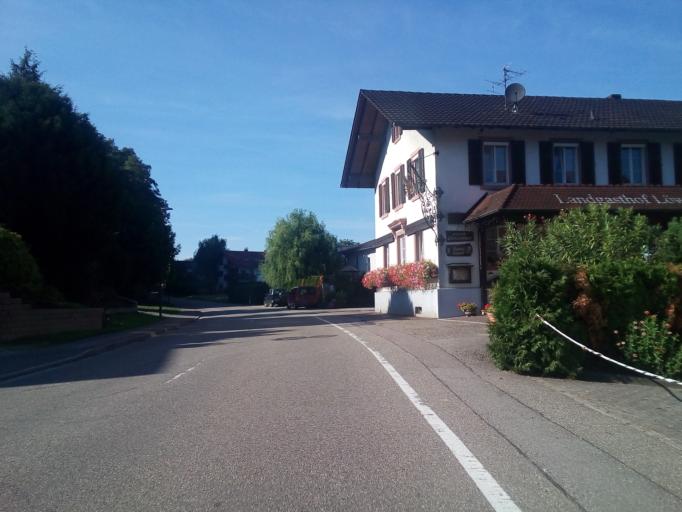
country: DE
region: Baden-Wuerttemberg
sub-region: Freiburg Region
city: Sasbach
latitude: 48.6317
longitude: 8.1045
